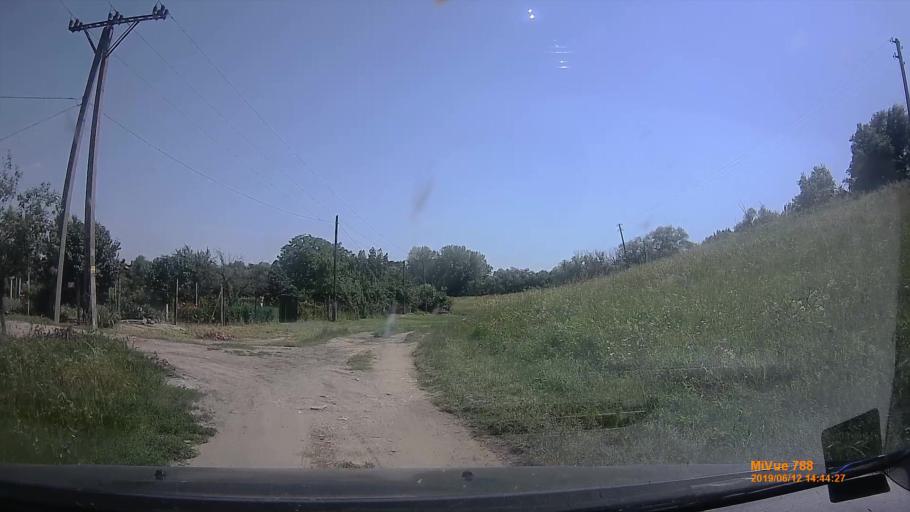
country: HU
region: Csongrad
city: Mako
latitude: 46.2034
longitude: 20.4673
